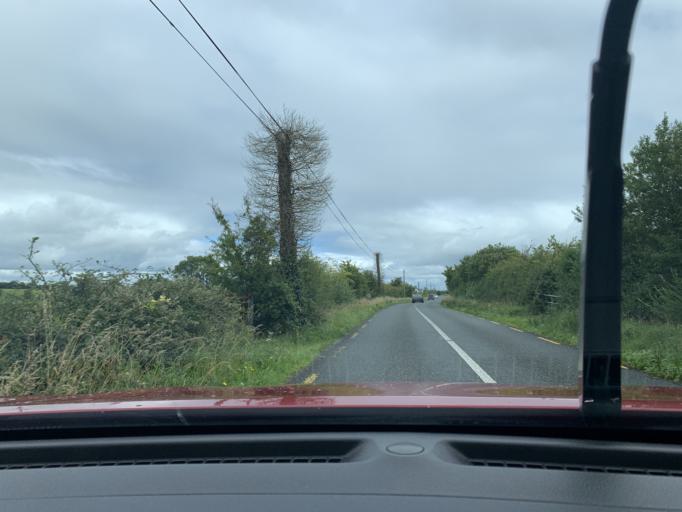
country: IE
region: Connaught
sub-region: County Leitrim
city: Carrick-on-Shannon
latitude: 53.8943
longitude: -8.1458
